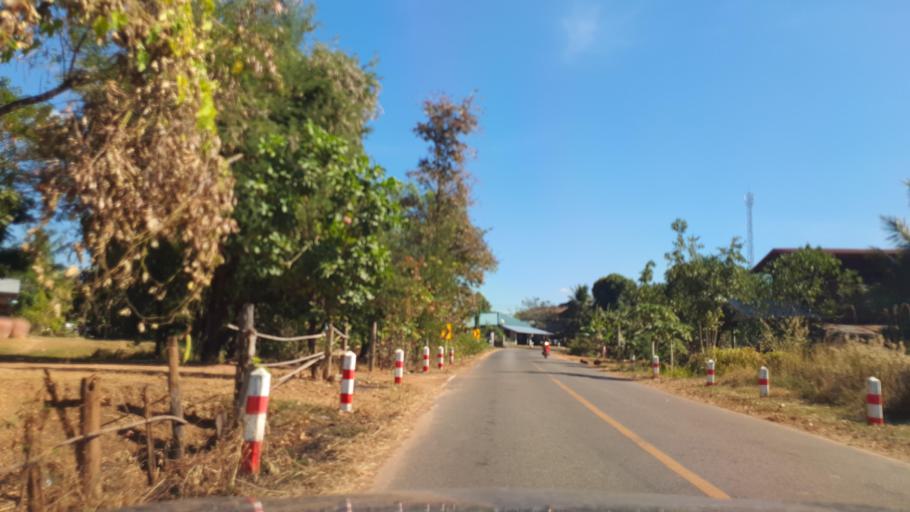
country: TH
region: Kalasin
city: Khao Wong
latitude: 16.7164
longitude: 104.1137
